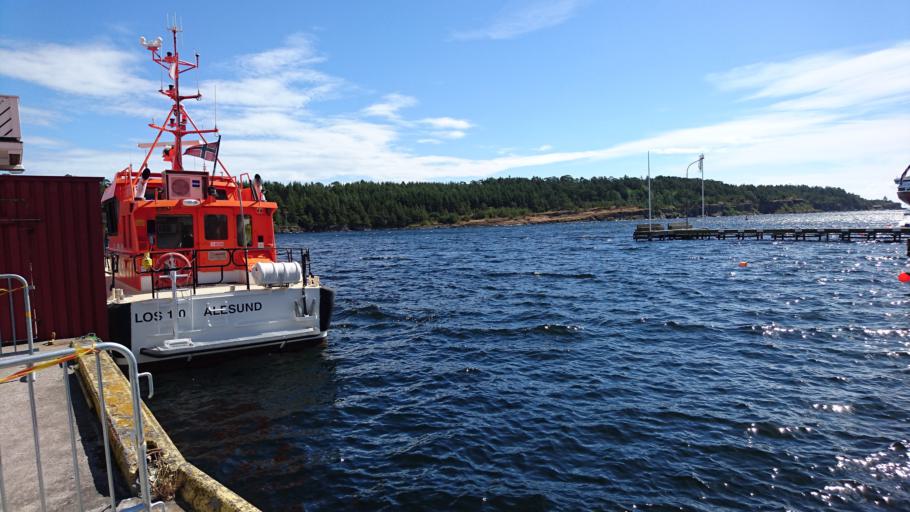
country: NO
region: Telemark
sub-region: Bamble
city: Langesund
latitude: 59.0008
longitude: 9.7501
